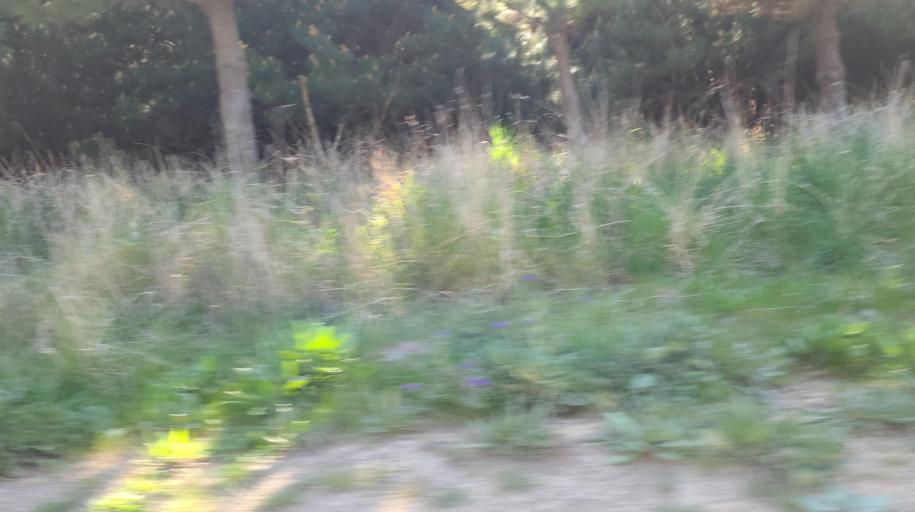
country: AU
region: New South Wales
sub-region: Blayney
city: Millthorpe
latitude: -33.4132
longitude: 149.3132
